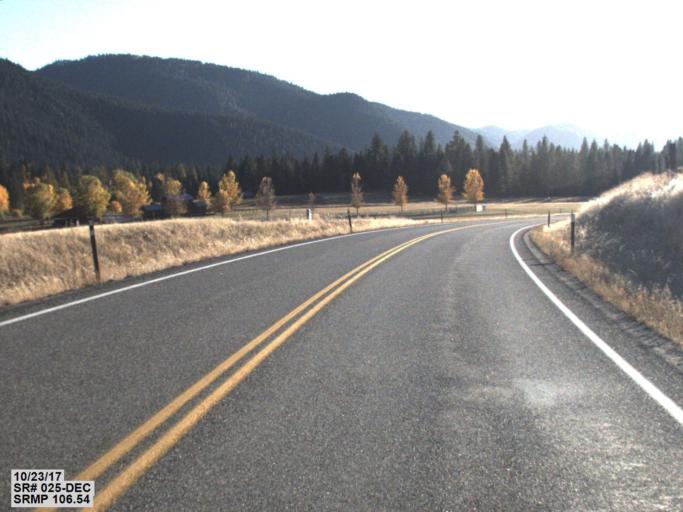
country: CA
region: British Columbia
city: Rossland
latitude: 48.8546
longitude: -117.8799
